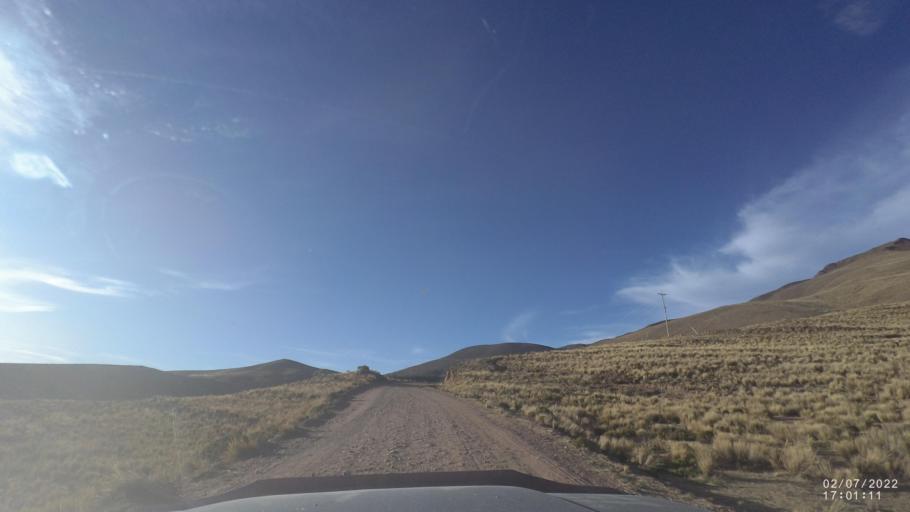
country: BO
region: Cochabamba
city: Irpa Irpa
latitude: -17.9331
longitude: -66.5557
